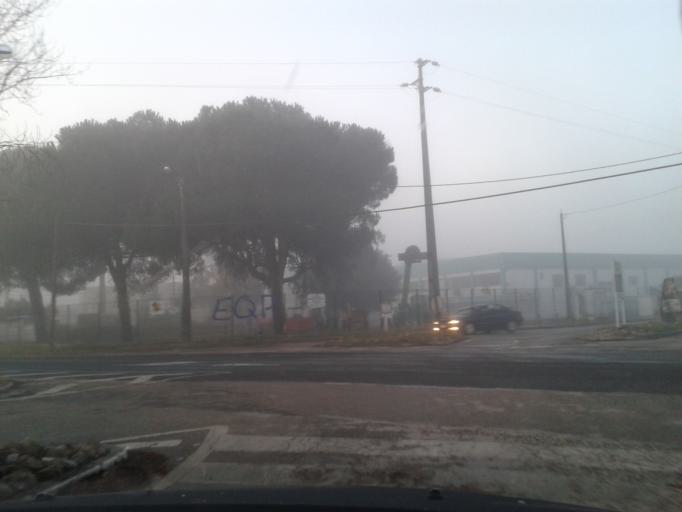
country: PT
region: Setubal
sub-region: Palmela
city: Palmela
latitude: 38.5986
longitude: -8.8963
